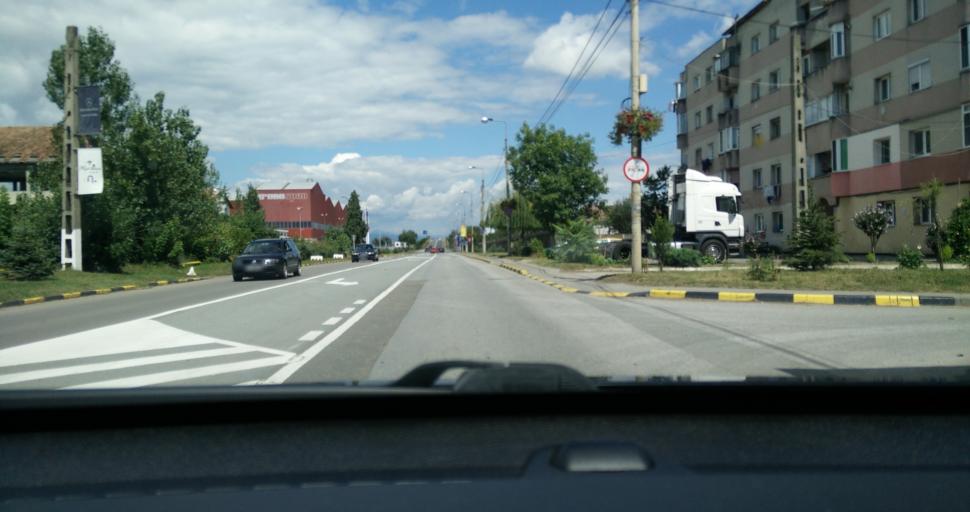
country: RO
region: Alba
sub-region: Municipiul Sebes
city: Sebes
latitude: 45.9674
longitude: 23.5576
